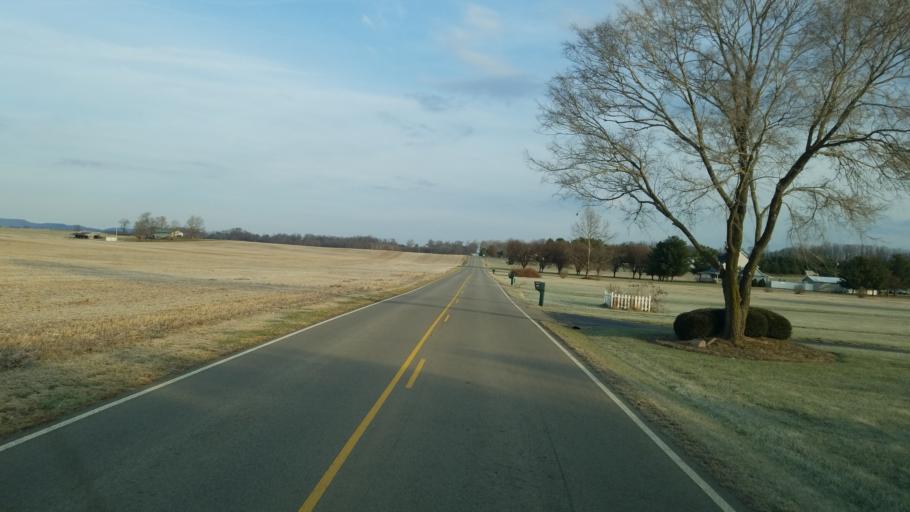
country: US
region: Ohio
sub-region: Ross County
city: Chillicothe
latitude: 39.2540
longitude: -82.8708
